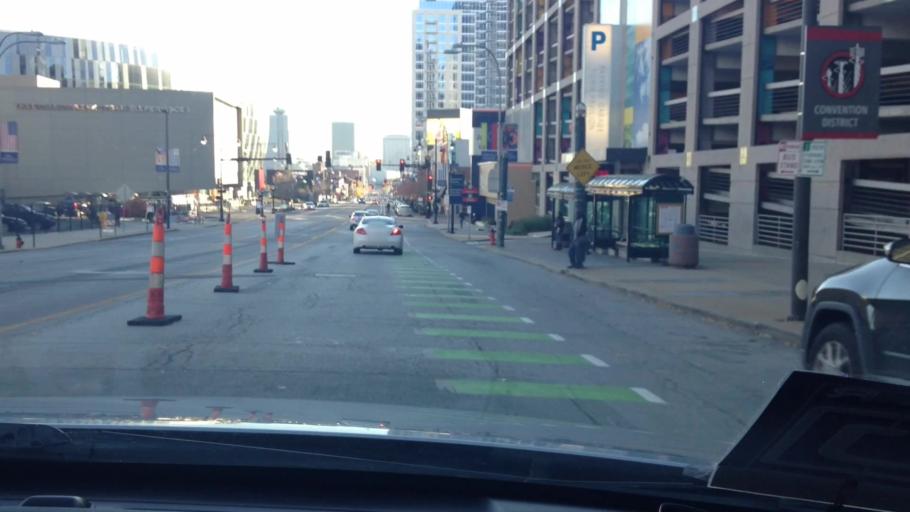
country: US
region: Missouri
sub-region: Jackson County
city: Kansas City
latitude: 39.0996
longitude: -94.5810
